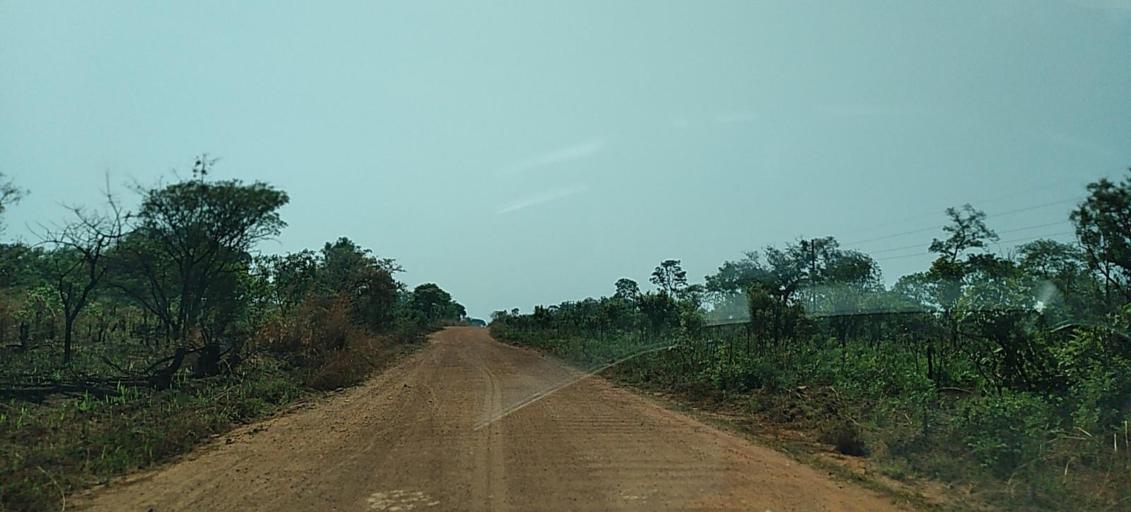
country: ZM
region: North-Western
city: Kansanshi
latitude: -12.0058
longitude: 26.5399
